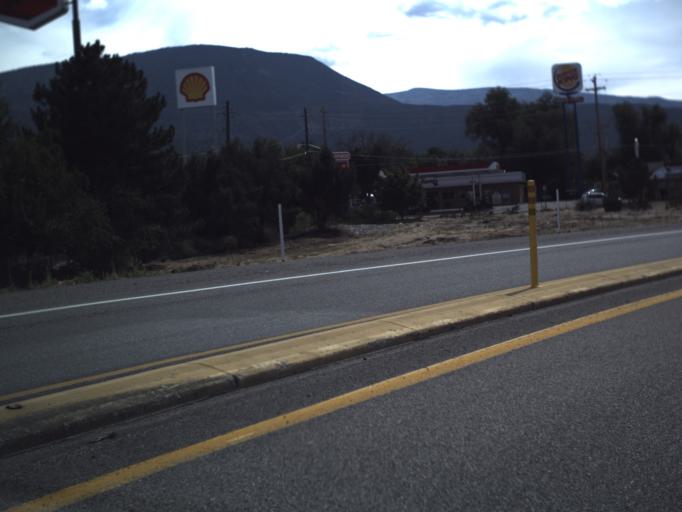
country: US
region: Utah
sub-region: Iron County
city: Cedar City
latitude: 37.6822
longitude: -113.0784
